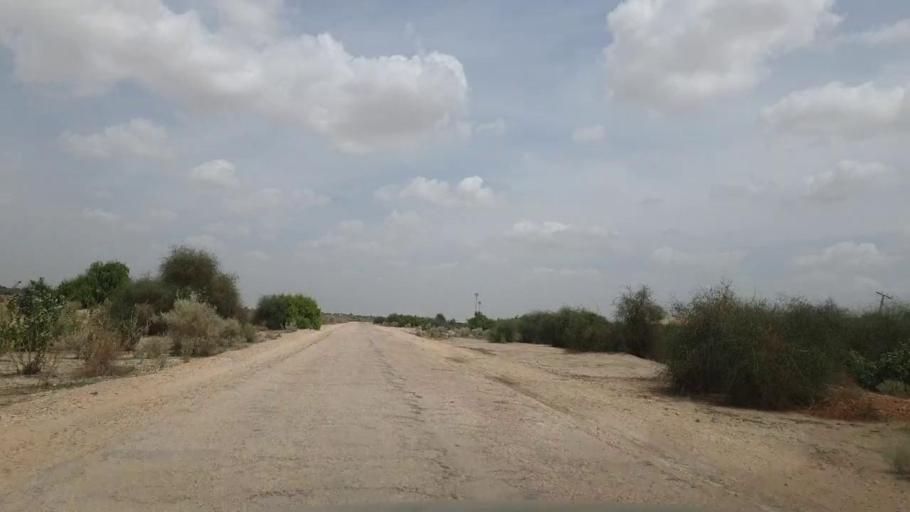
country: PK
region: Sindh
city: Kot Diji
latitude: 27.2029
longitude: 69.1459
